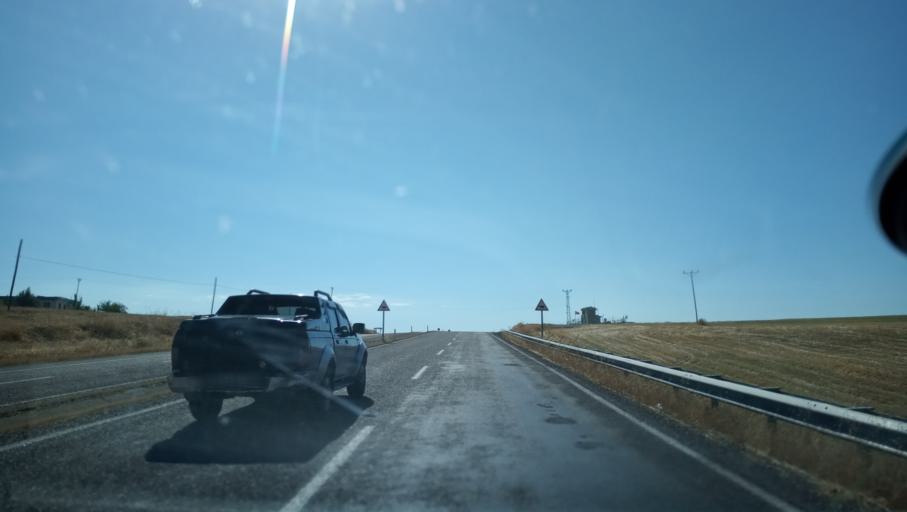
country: TR
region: Diyarbakir
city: Bagdere
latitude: 38.1292
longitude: 40.7746
